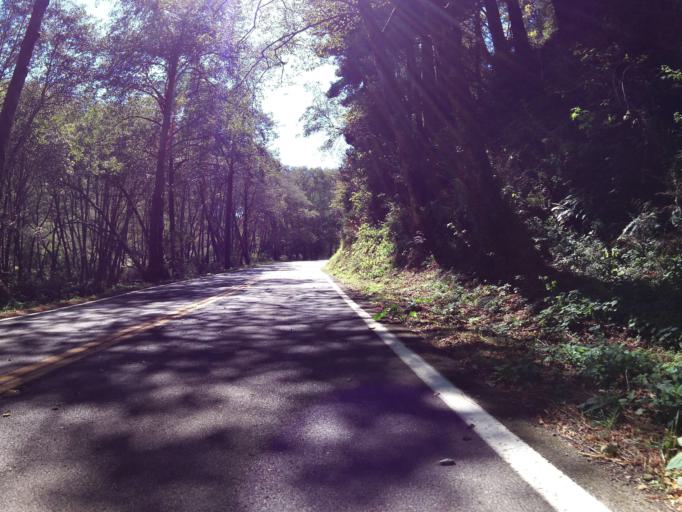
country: US
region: California
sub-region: Mendocino County
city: Fort Bragg
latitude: 39.7787
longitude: -123.8325
